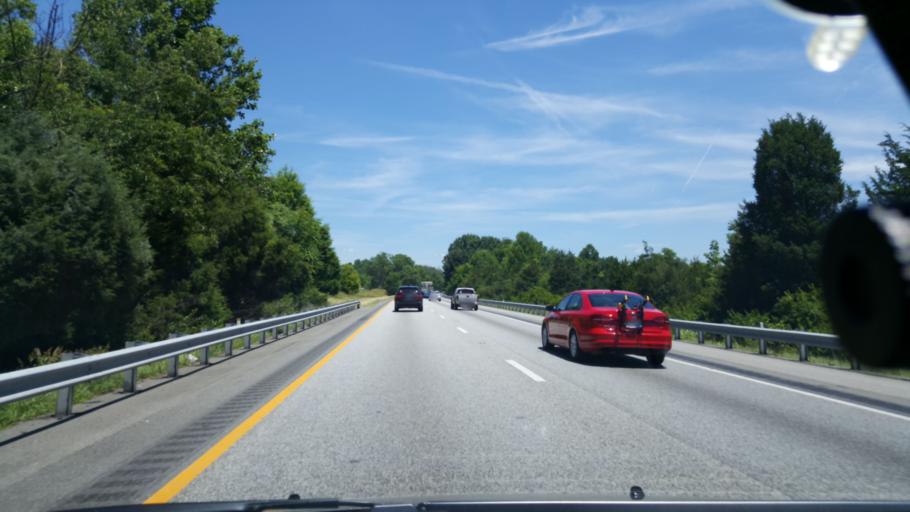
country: US
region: Virginia
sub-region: Botetourt County
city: Daleville
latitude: 37.4387
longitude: -79.8678
